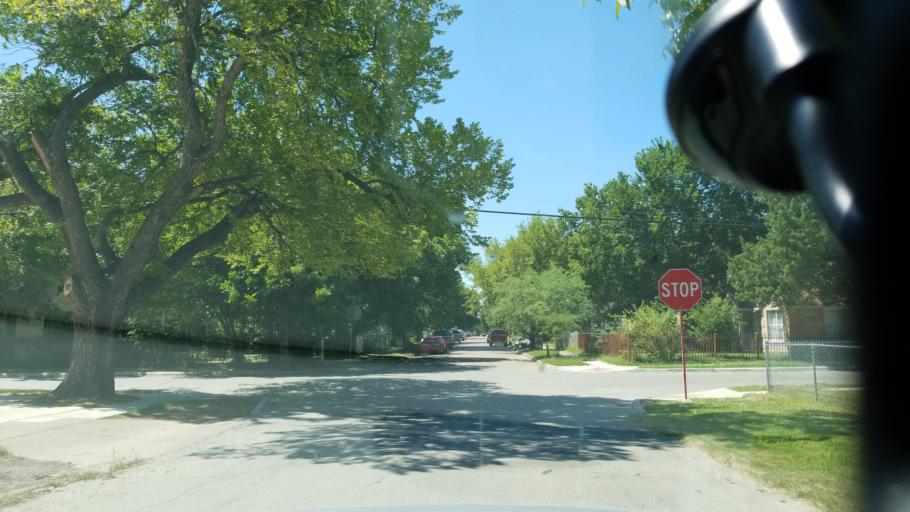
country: US
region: Texas
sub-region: Dallas County
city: Dallas
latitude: 32.7098
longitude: -96.8171
